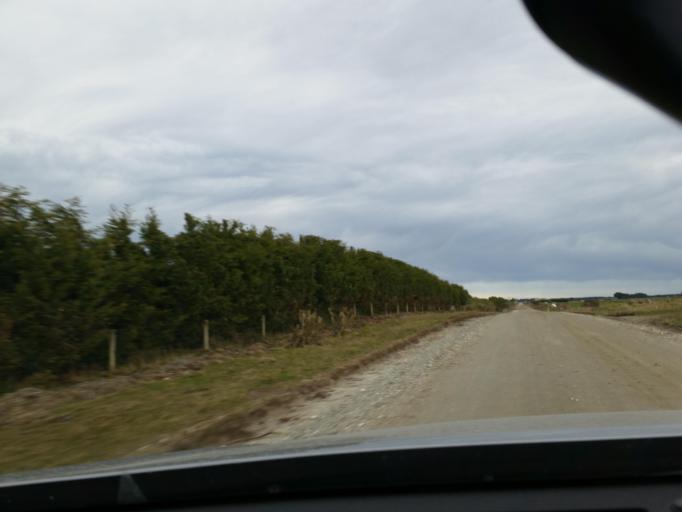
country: NZ
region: Southland
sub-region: Invercargill City
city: Invercargill
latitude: -46.4359
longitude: 168.5062
